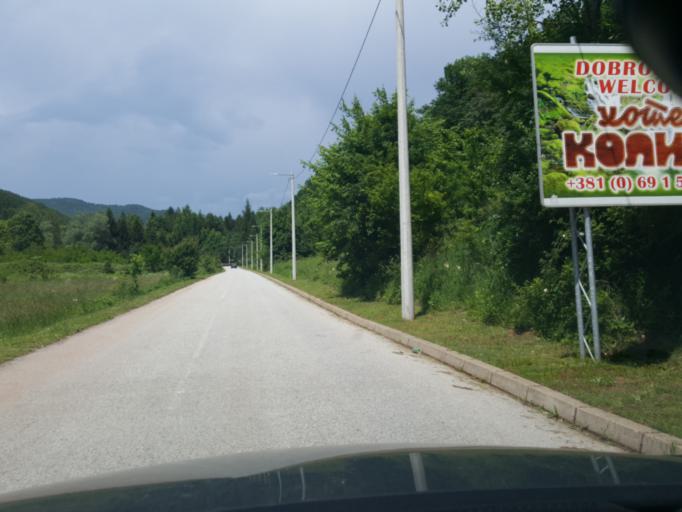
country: RS
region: Central Serbia
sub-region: Nisavski Okrug
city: Razanj
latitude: 43.8603
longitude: 21.6247
